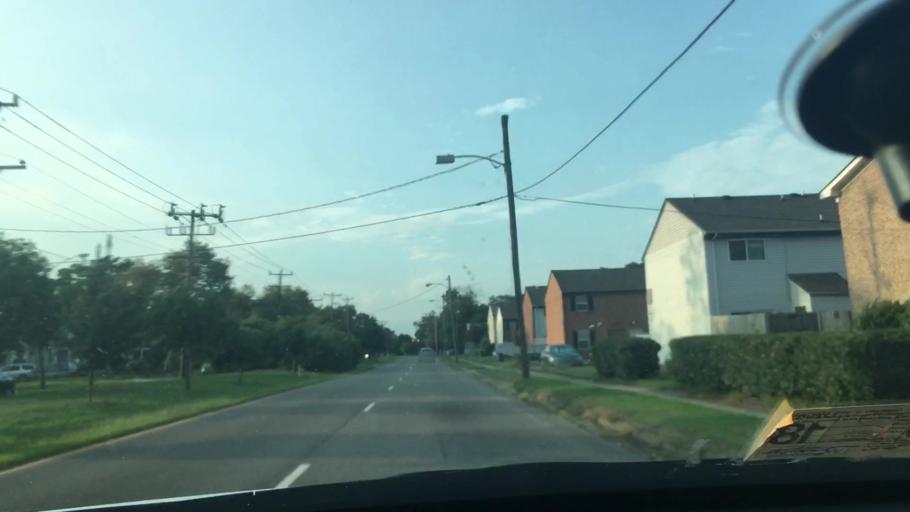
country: US
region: Virginia
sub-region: City of Norfolk
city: Norfolk
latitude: 36.9309
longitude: -76.2439
